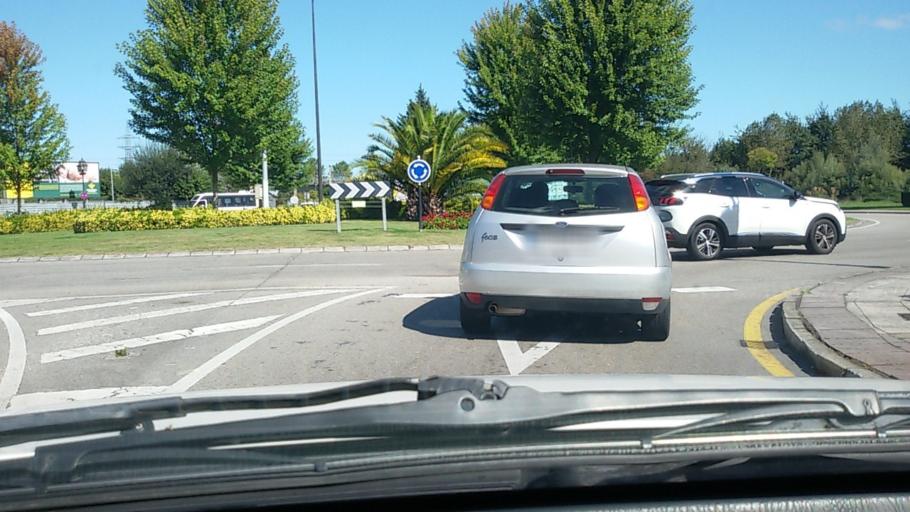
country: ES
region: Asturias
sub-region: Province of Asturias
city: Lugones
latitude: 43.3899
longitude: -5.8199
